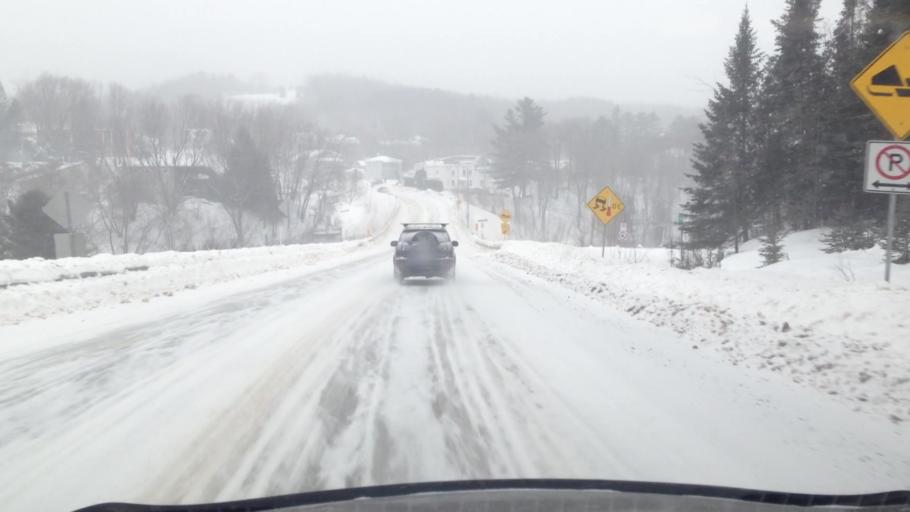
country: CA
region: Quebec
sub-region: Laurentides
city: Mont-Tremblant
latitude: 45.9734
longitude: -74.6317
